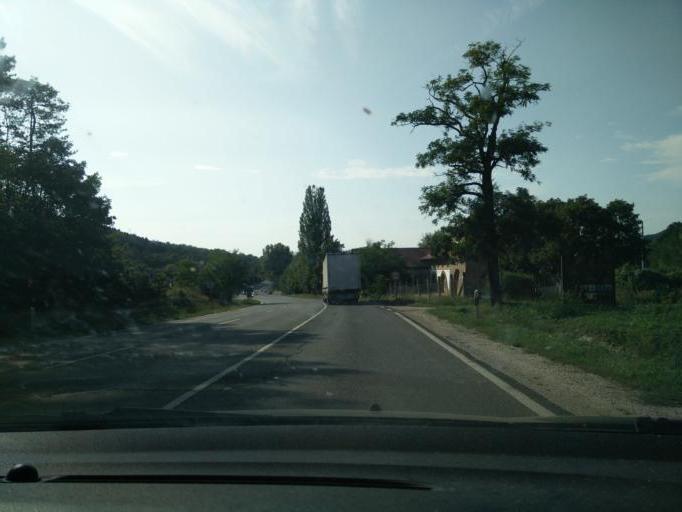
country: HU
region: Pest
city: Piliscsaba
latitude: 47.6281
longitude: 18.8552
